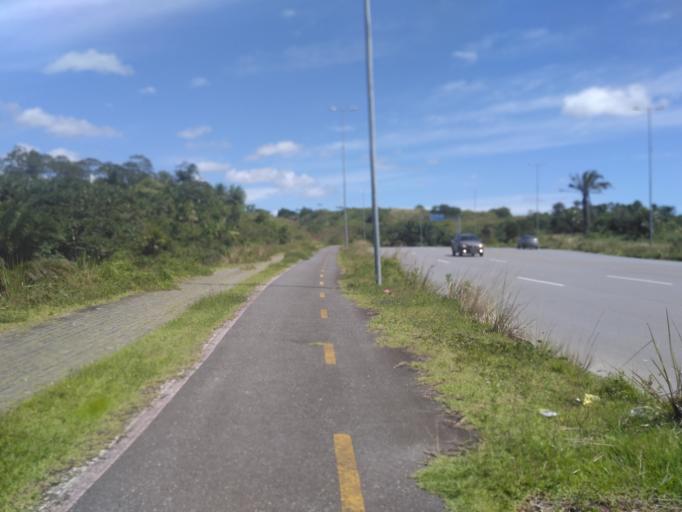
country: BR
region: Pernambuco
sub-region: Sao Lourenco Da Mata
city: Sao Lourenco da Mata
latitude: -8.0425
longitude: -34.9956
